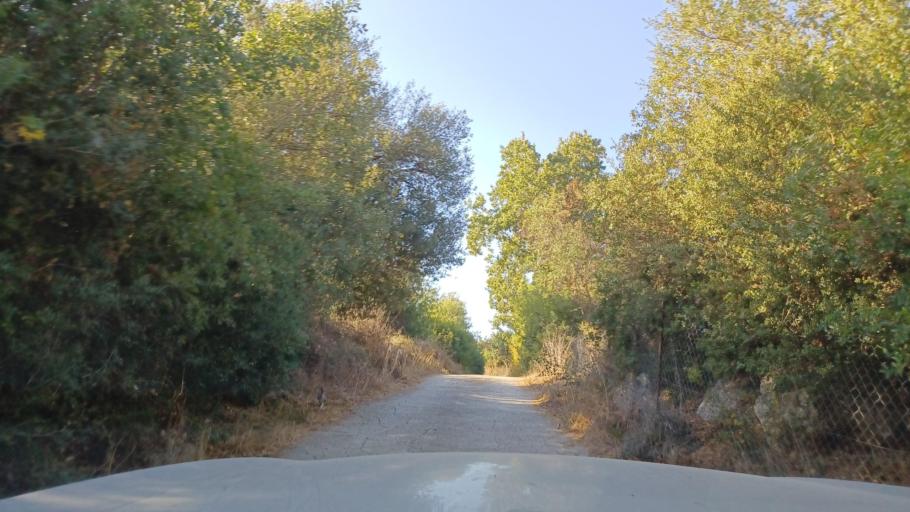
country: CY
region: Pafos
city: Polis
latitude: 34.9971
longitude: 32.4879
